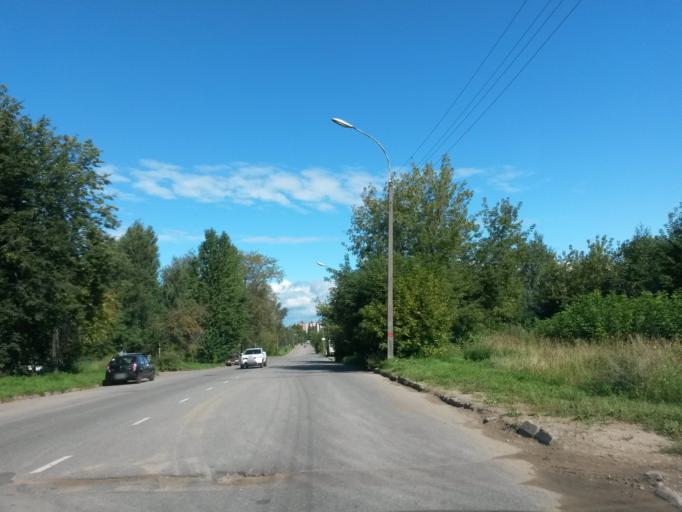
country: RU
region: Jaroslavl
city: Yaroslavl
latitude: 57.5814
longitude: 39.8658
